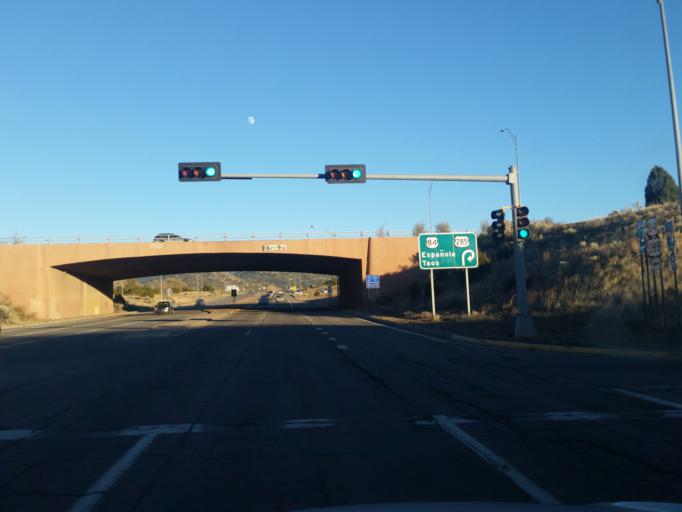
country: US
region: New Mexico
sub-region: Santa Fe County
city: Santa Fe
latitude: 35.6591
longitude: -105.9577
